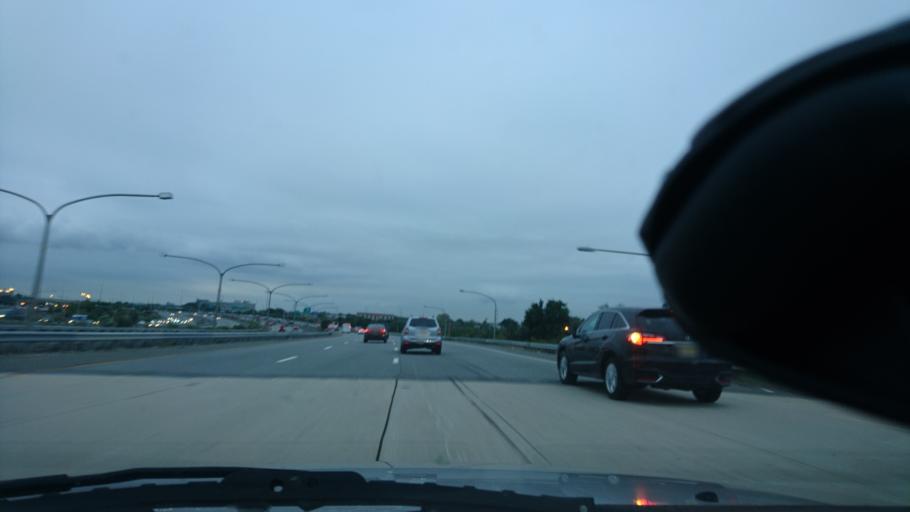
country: US
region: Pennsylvania
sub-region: Delaware County
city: Colwyn
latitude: 39.8926
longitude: -75.2361
